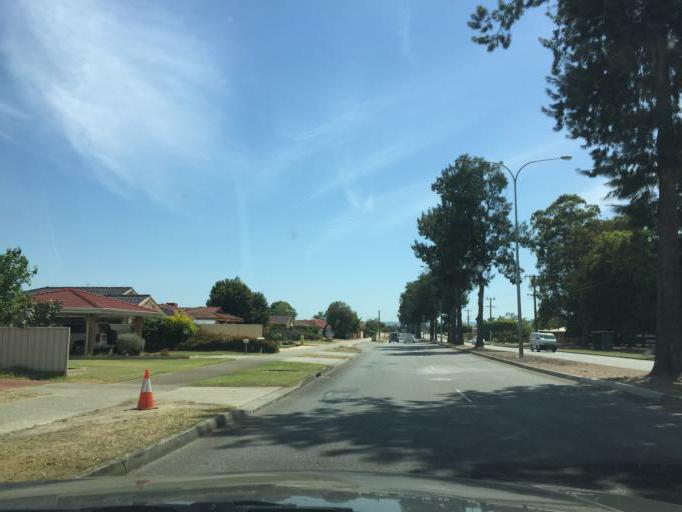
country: AU
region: Western Australia
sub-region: Gosnells
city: Thornlie
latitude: -32.0744
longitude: 115.9621
